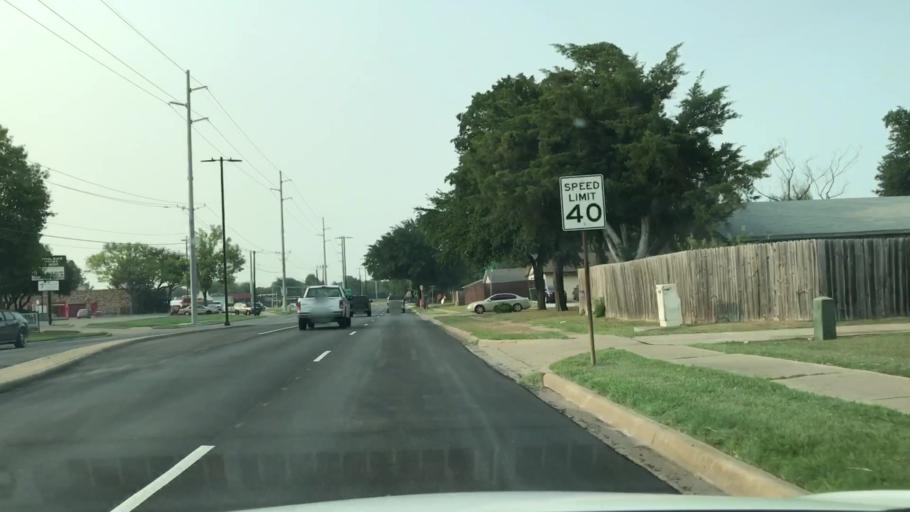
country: US
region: Texas
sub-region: Dallas County
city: Garland
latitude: 32.9264
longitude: -96.6137
